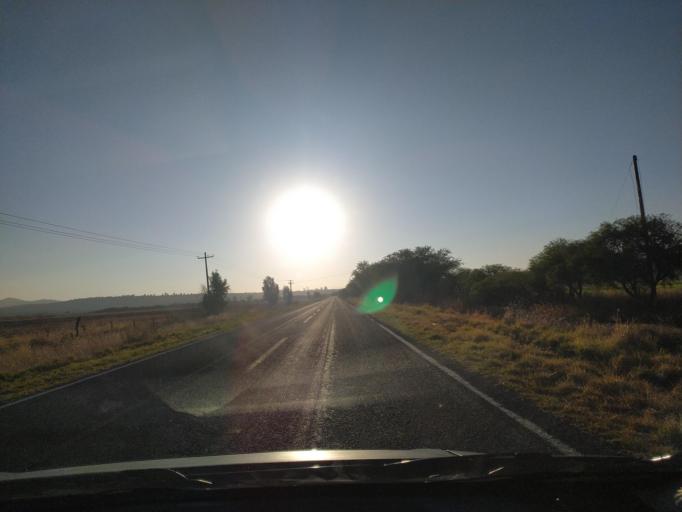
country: MX
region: Guanajuato
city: Ciudad Manuel Doblado
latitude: 20.7356
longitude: -101.8443
